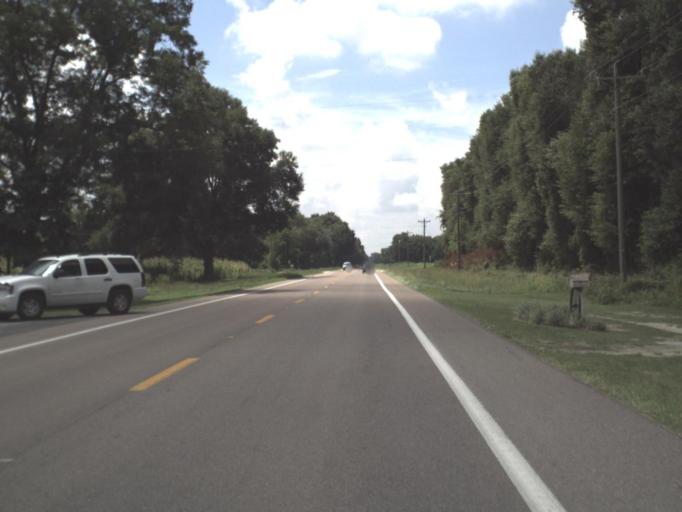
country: US
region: Florida
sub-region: Gilchrist County
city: Trenton
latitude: 29.7066
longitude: -82.8575
